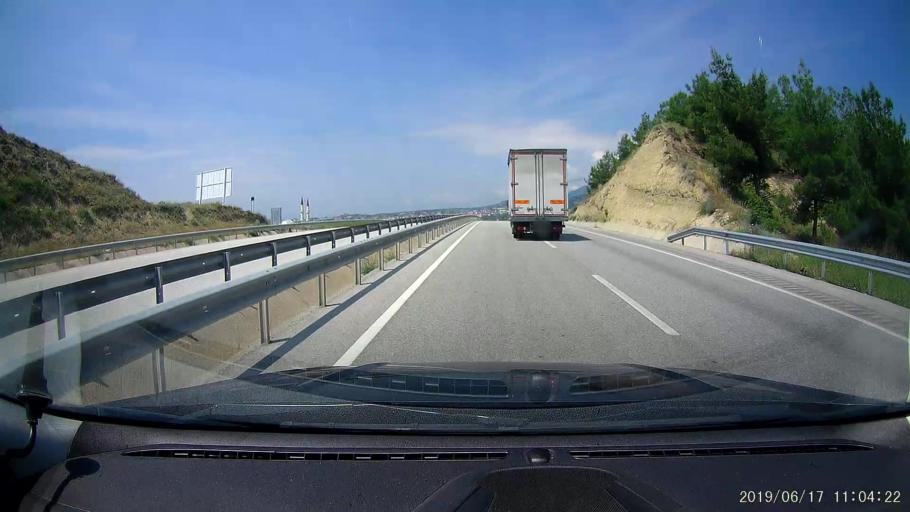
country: TR
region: Kastamonu
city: Tosya
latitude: 41.0203
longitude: 34.0961
